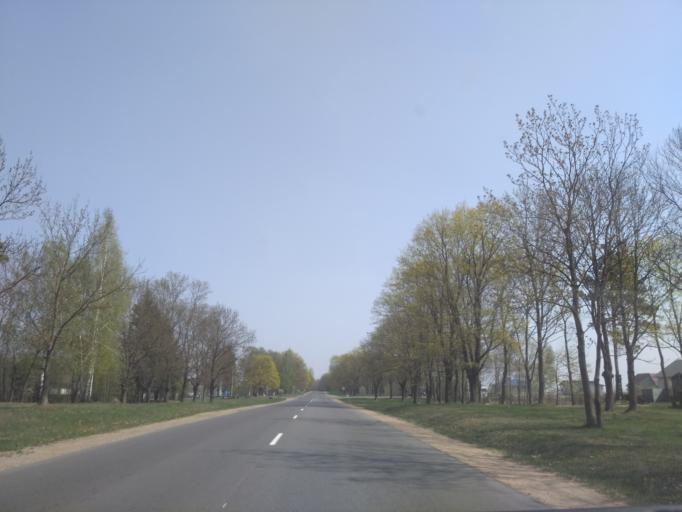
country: BY
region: Minsk
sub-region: Smalyavitski Rayon
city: Oktjabr'skij
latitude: 54.0280
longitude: 28.2050
